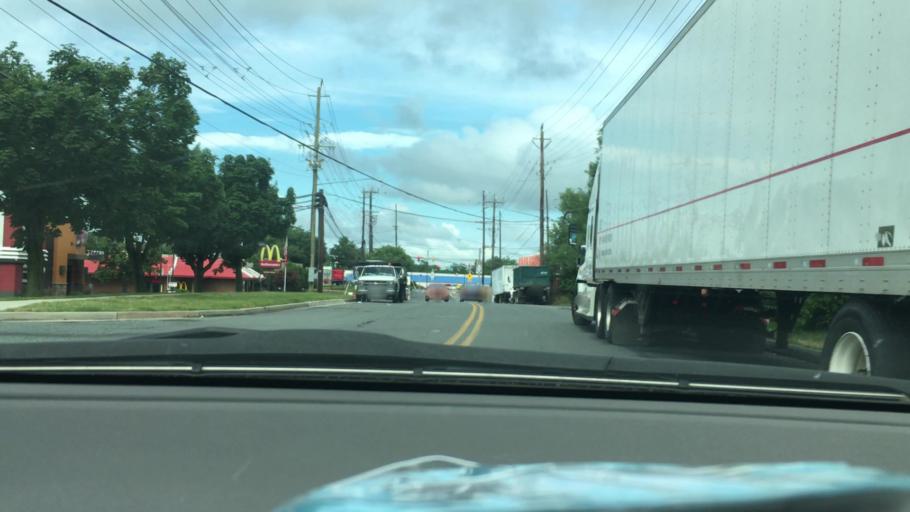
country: US
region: Maryland
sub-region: Montgomery County
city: Germantown
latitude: 39.1779
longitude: -77.2407
